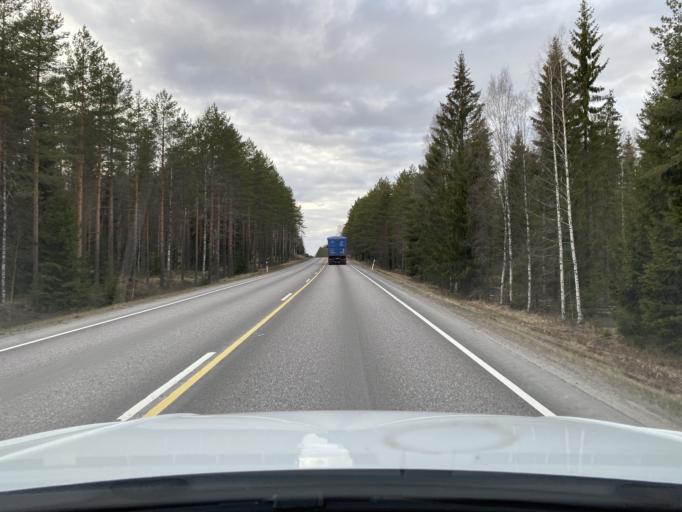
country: FI
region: Uusimaa
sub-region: Helsinki
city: Kaerkoelae
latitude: 60.8176
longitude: 24.0423
